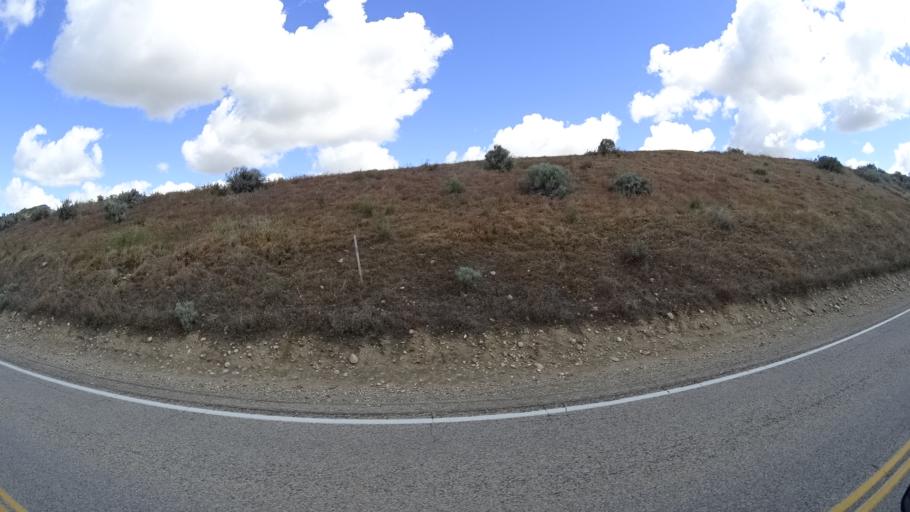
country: US
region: Idaho
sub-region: Ada County
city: Garden City
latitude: 43.4906
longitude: -116.2658
